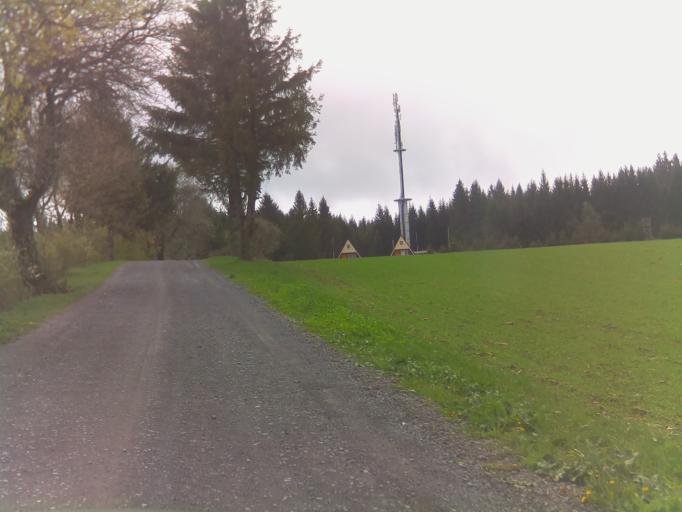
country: DE
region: Thuringia
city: Grossbreitenbach
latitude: 50.5771
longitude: 11.0185
